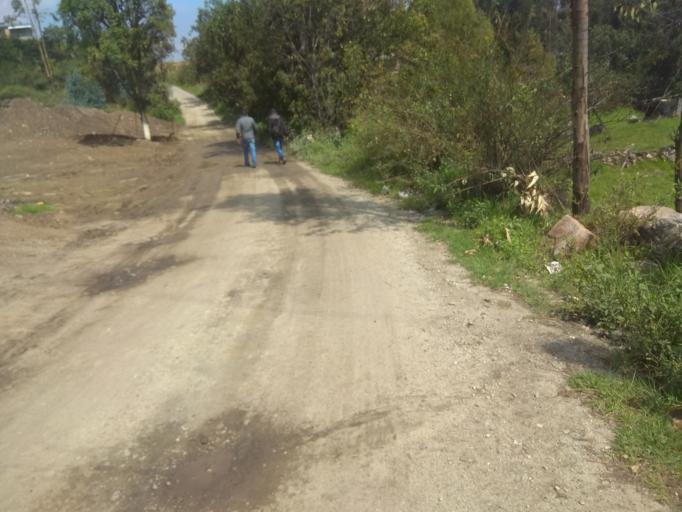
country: CO
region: Boyaca
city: Socha Viejo
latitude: 5.9835
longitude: -72.7149
